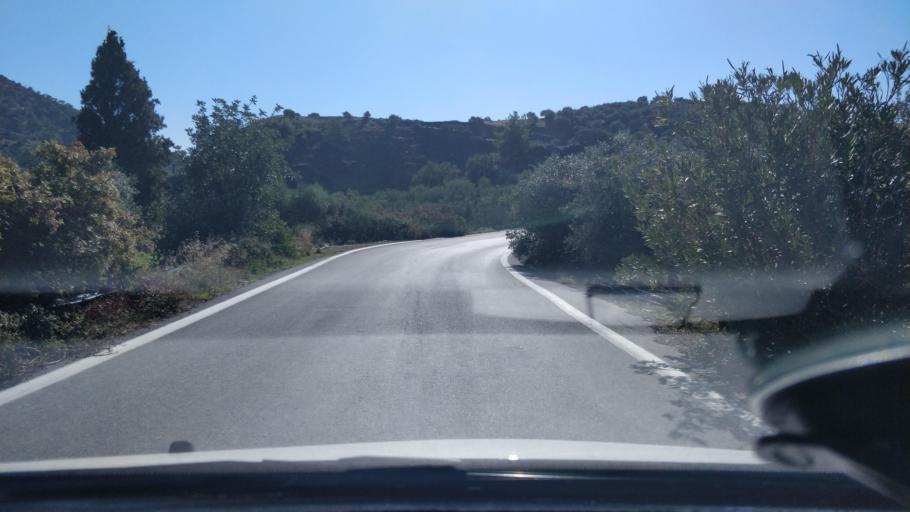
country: GR
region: Crete
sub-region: Nomos Irakleiou
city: Kastelli
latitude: 35.0189
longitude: 25.4492
